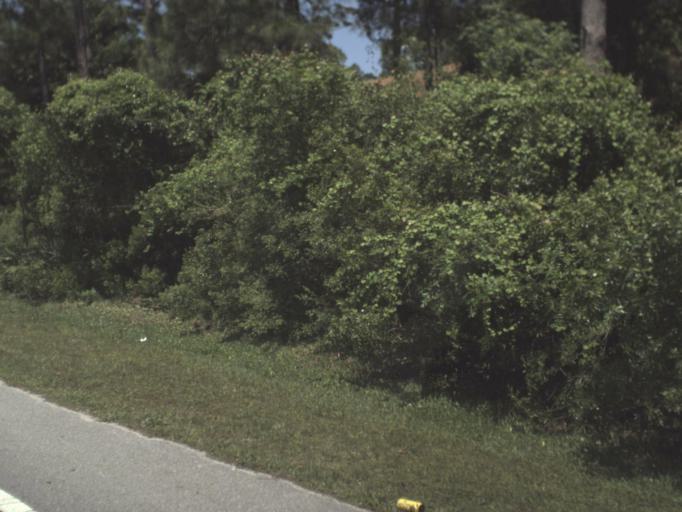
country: US
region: Florida
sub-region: Bay County
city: Pretty Bayou
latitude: 30.1798
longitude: -85.6837
